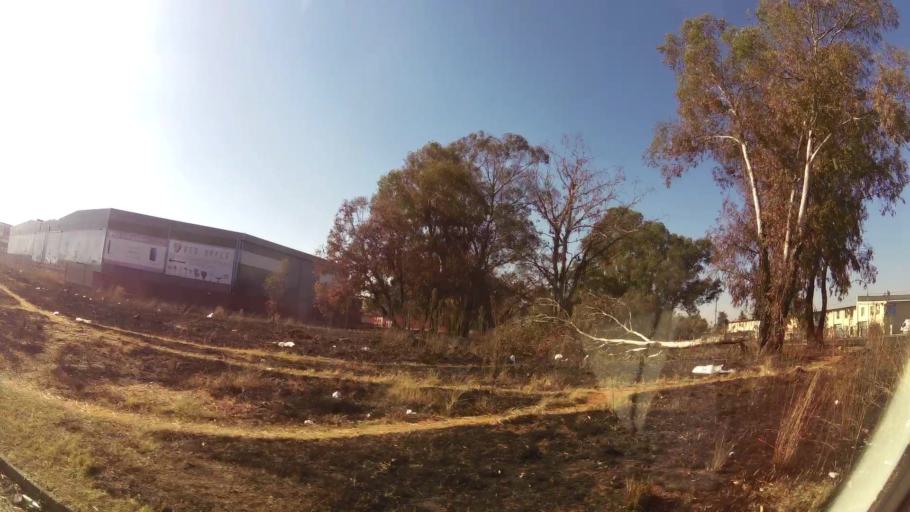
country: ZA
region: Gauteng
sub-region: City of Johannesburg Metropolitan Municipality
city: Johannesburg
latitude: -26.2311
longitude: 28.0893
